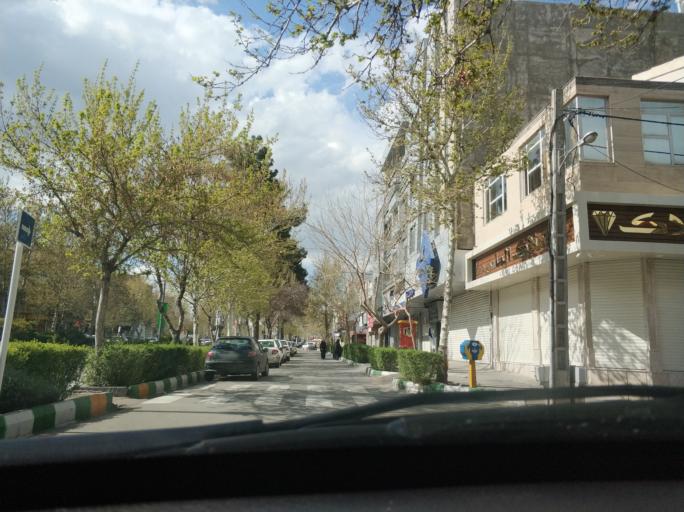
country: IR
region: Razavi Khorasan
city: Mashhad
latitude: 36.2731
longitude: 59.5939
